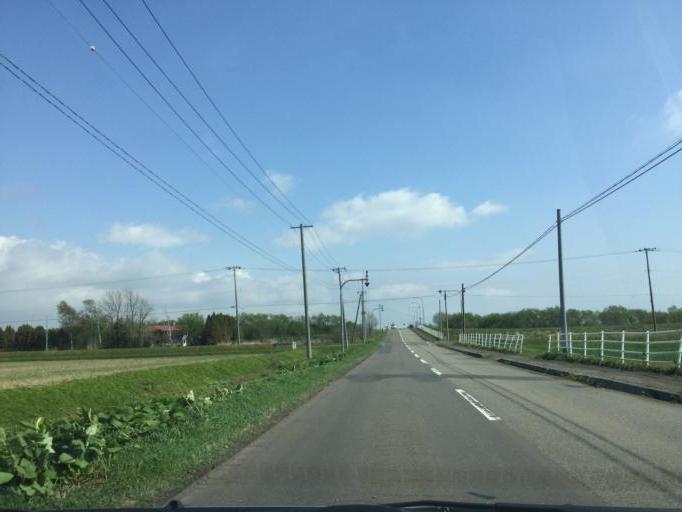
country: JP
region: Hokkaido
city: Iwamizawa
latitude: 43.1476
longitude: 141.7190
